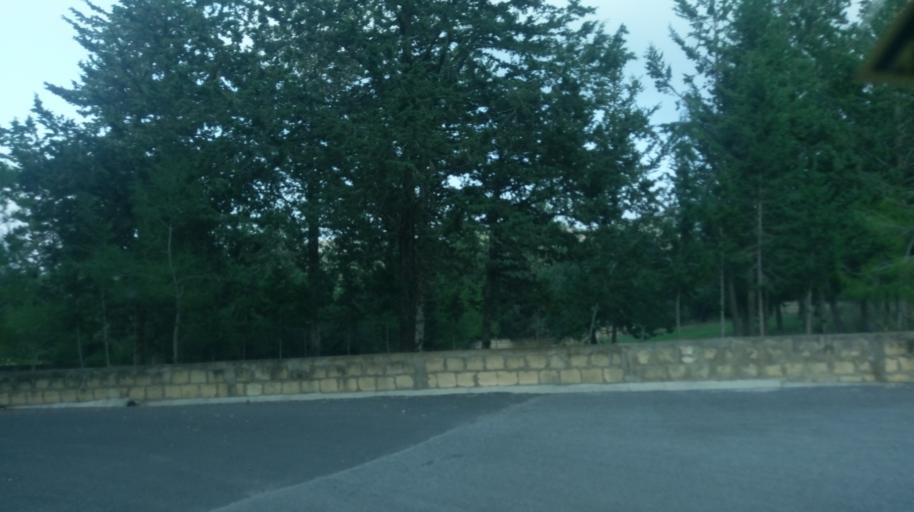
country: CY
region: Ammochostos
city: Trikomo
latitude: 35.3933
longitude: 33.8601
